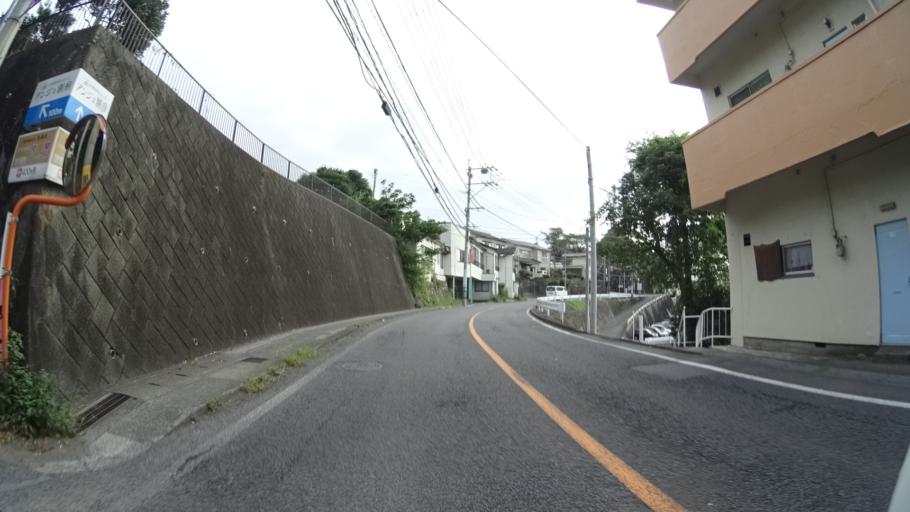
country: JP
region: Oita
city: Beppu
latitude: 33.3173
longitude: 131.4768
